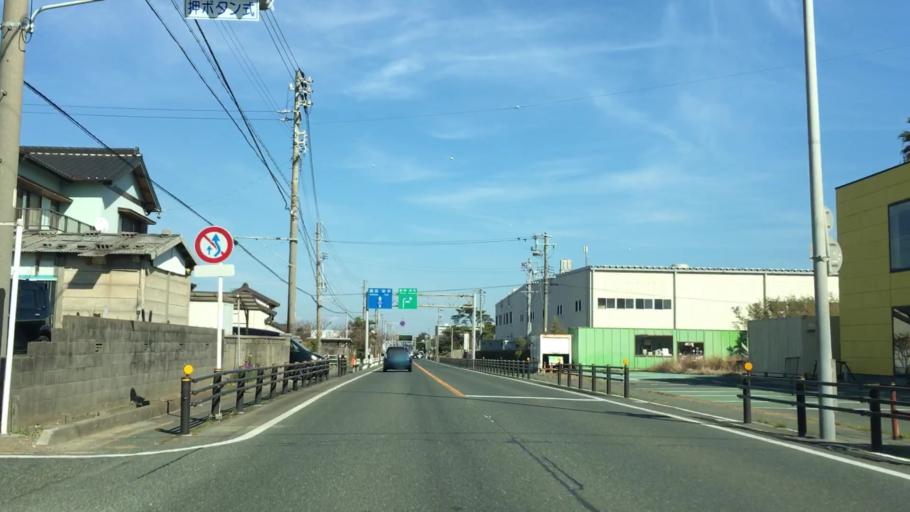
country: JP
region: Shizuoka
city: Kosai-shi
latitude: 34.6800
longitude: 137.5278
